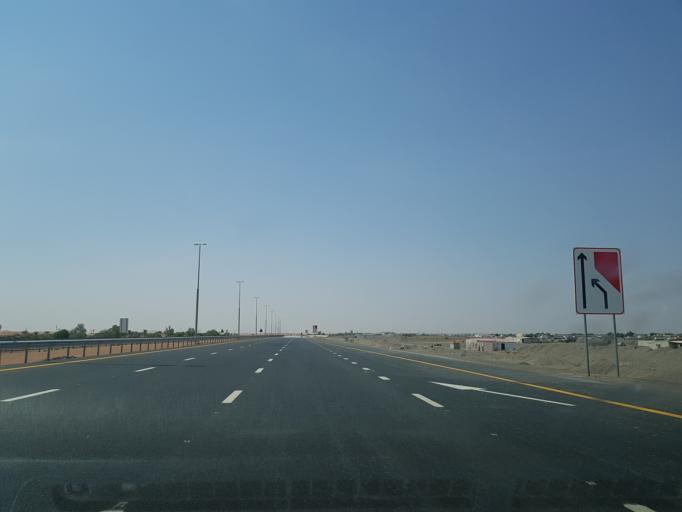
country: AE
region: Ash Shariqah
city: Adh Dhayd
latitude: 25.2333
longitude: 55.9103
